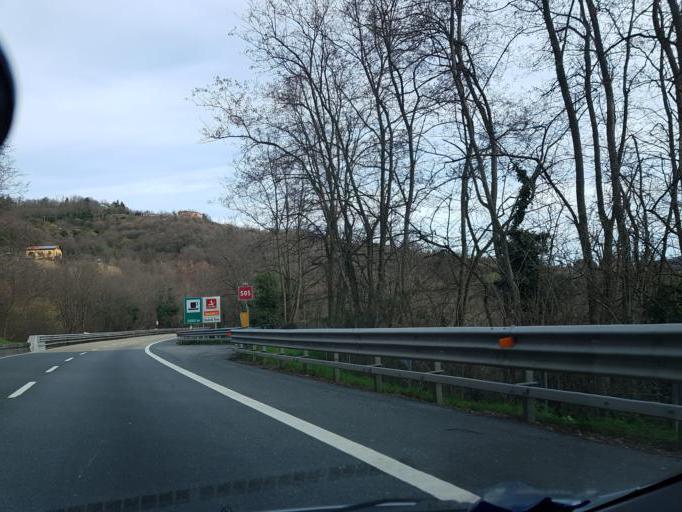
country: IT
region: Liguria
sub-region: Provincia di Genova
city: Pedemonte
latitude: 44.5113
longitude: 8.9263
